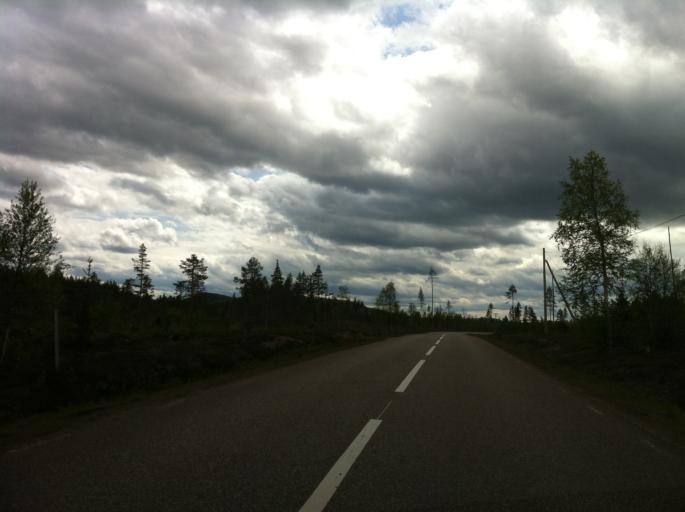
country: NO
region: Hedmark
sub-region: Trysil
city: Innbygda
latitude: 61.4336
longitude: 13.0962
